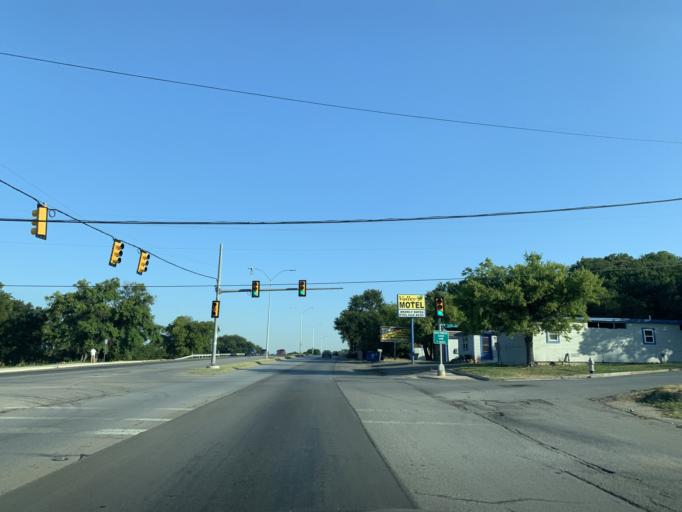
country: US
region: Texas
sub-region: Tarrant County
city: River Oaks
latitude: 32.7755
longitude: -97.3671
